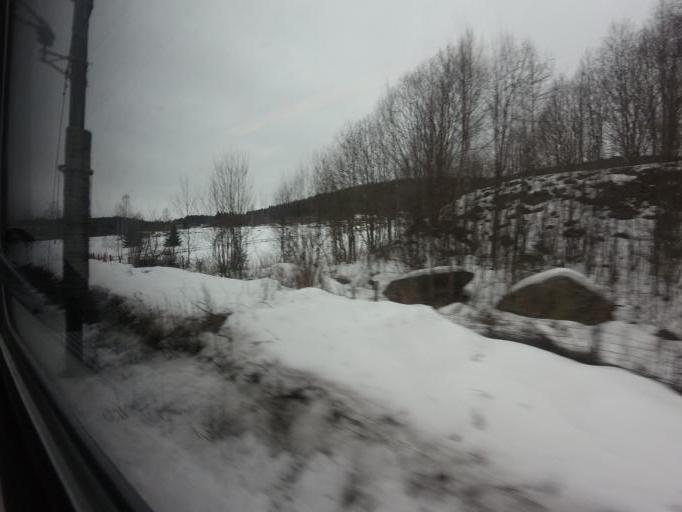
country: NO
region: Hedmark
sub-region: Ringsaker
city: Moelv
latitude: 60.9157
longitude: 10.7713
